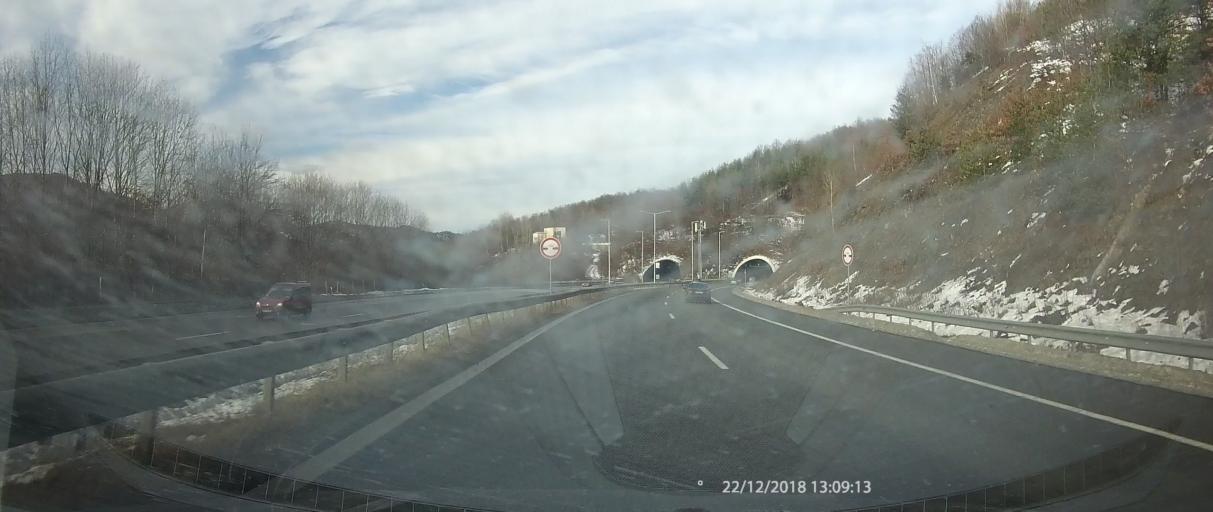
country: BG
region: Sofiya
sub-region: Obshtina Botevgrad
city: Botevgrad
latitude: 42.8513
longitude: 23.7908
